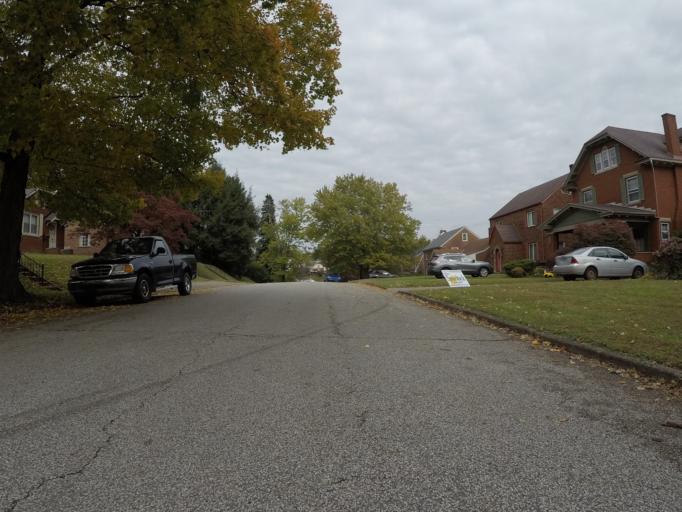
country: US
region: West Virginia
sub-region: Cabell County
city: Huntington
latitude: 38.4063
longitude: -82.4088
